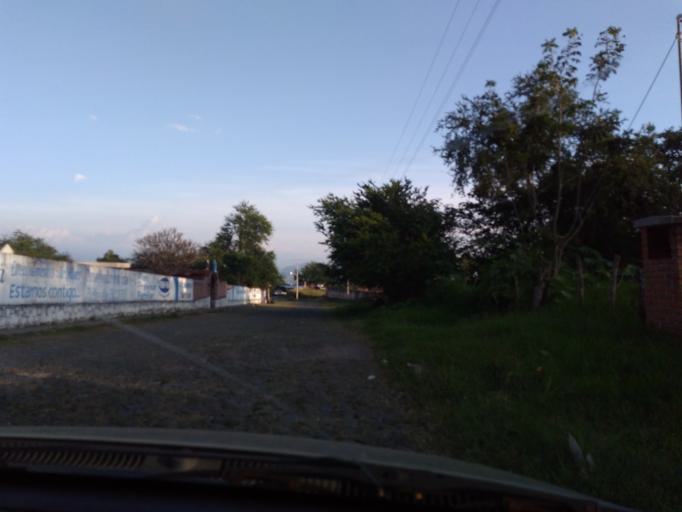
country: MX
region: Jalisco
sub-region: Tonila
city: San Marcos
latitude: 19.4482
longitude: -103.5101
